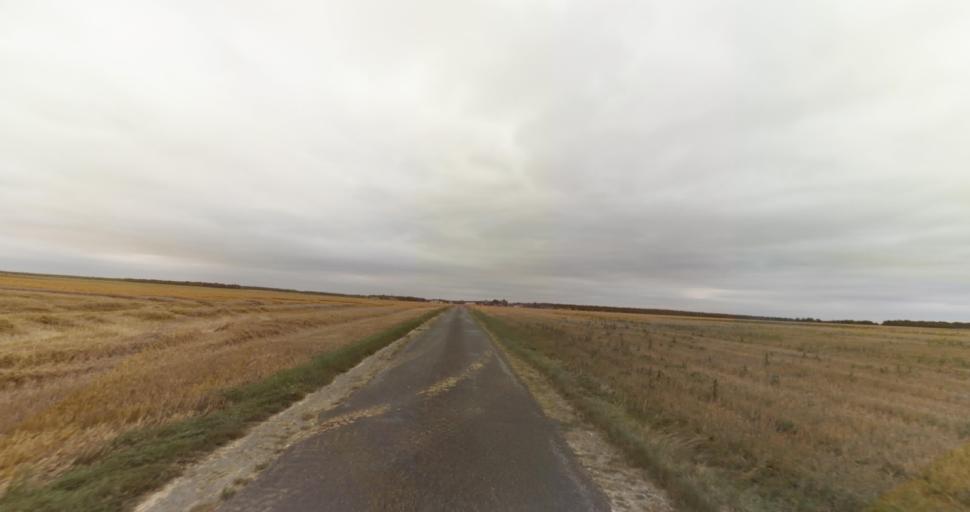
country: FR
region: Haute-Normandie
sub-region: Departement de l'Eure
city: La Couture-Boussey
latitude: 48.9208
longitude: 1.3931
